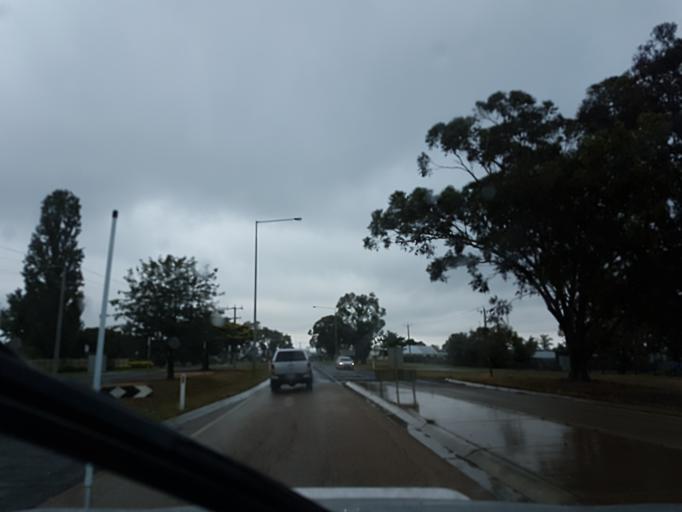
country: AU
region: Victoria
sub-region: East Gippsland
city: Bairnsdale
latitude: -37.8093
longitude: 147.6483
